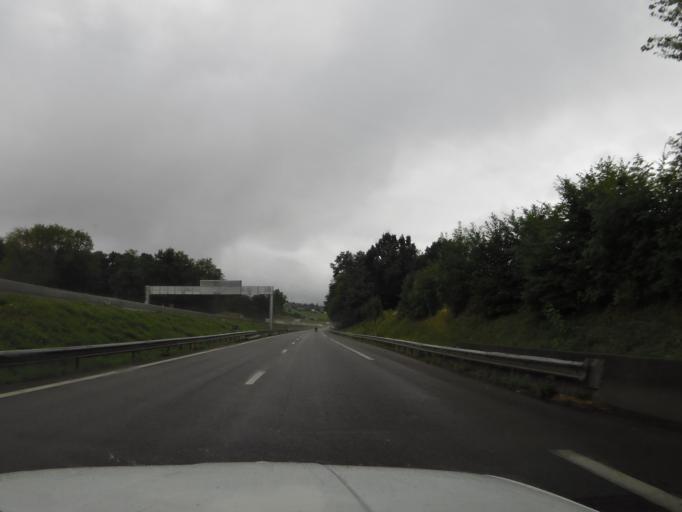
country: FR
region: Rhone-Alpes
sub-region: Departement de la Savoie
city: La Motte-Servolex
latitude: 45.5939
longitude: 5.8563
